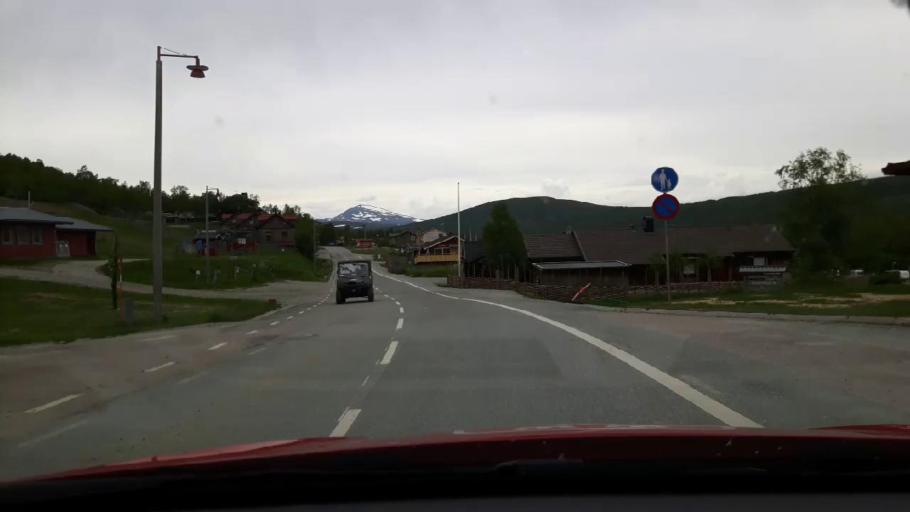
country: NO
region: Sor-Trondelag
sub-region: Tydal
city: Aas
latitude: 62.7013
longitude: 12.3886
